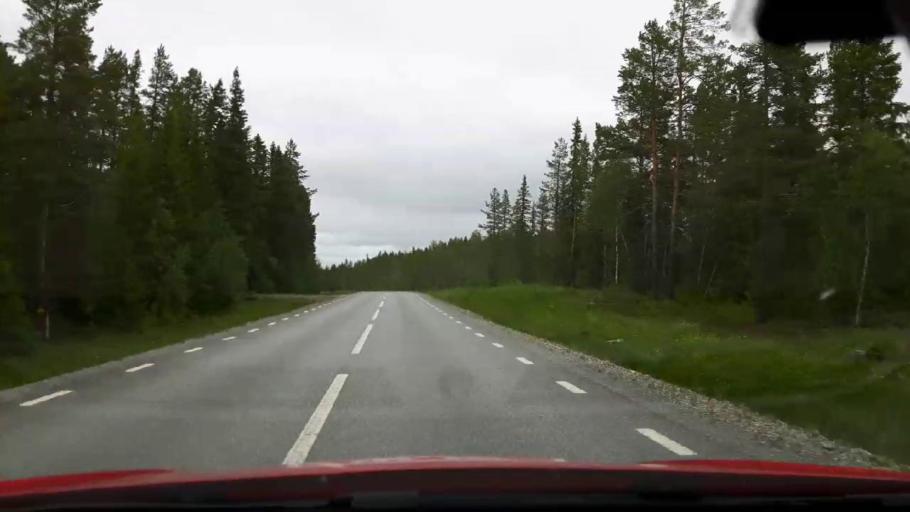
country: SE
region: Jaemtland
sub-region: OEstersunds Kommun
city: Lit
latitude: 63.6934
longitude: 14.6821
